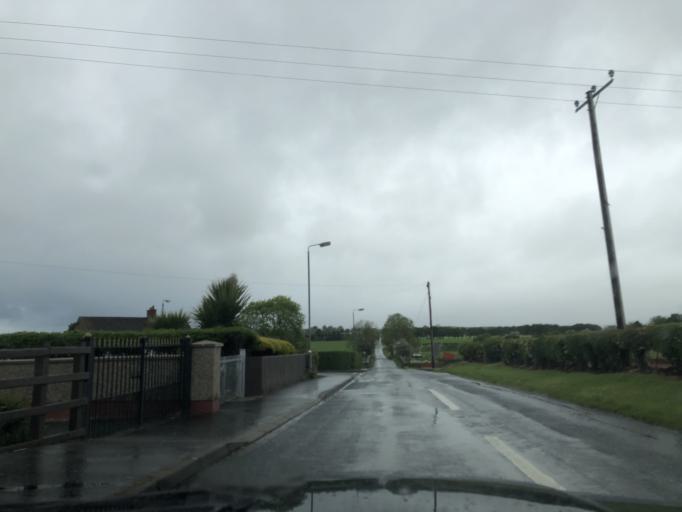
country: GB
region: Northern Ireland
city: Dunloy
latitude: 55.1232
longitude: -6.3625
